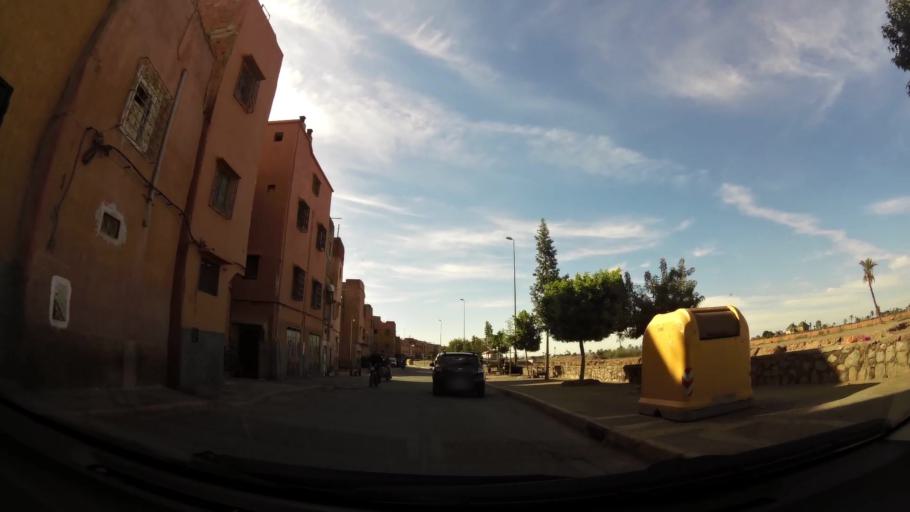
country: MA
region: Marrakech-Tensift-Al Haouz
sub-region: Marrakech
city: Marrakesh
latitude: 31.6162
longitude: -7.9630
